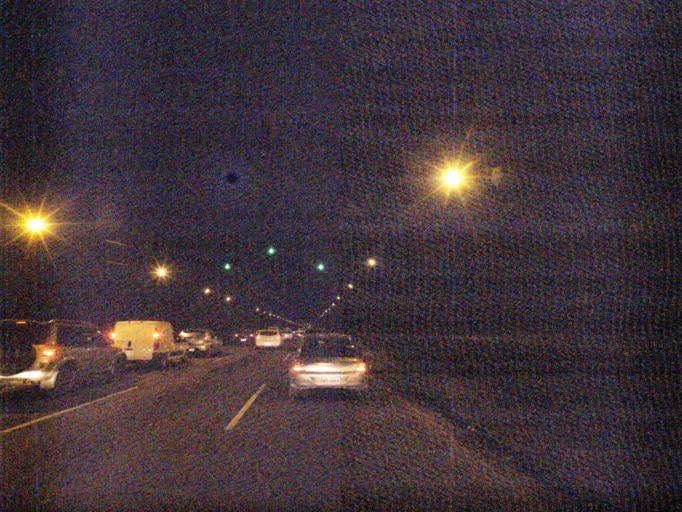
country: BR
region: Rio de Janeiro
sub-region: Rio De Janeiro
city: Rio de Janeiro
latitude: -22.9462
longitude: -43.2034
